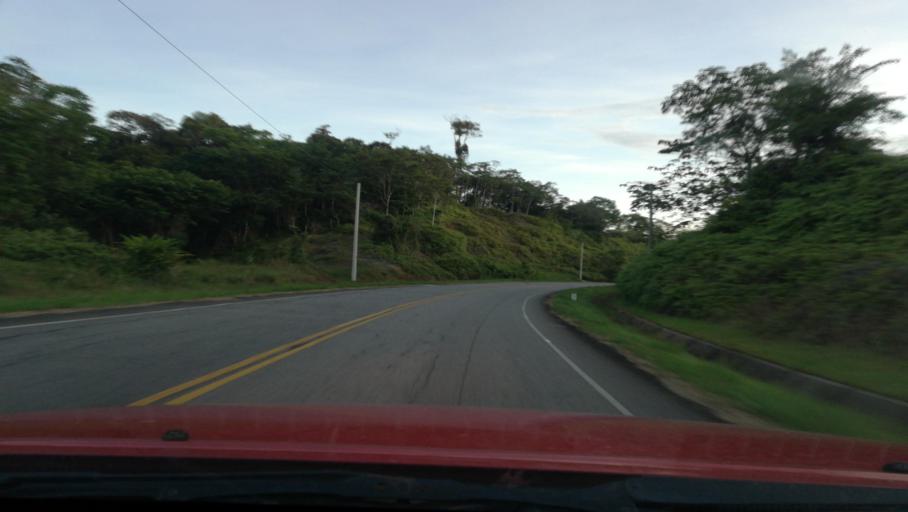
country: PE
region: Loreto
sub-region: Provincia de Loreto
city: Nauta
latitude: -4.4028
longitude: -73.5756
